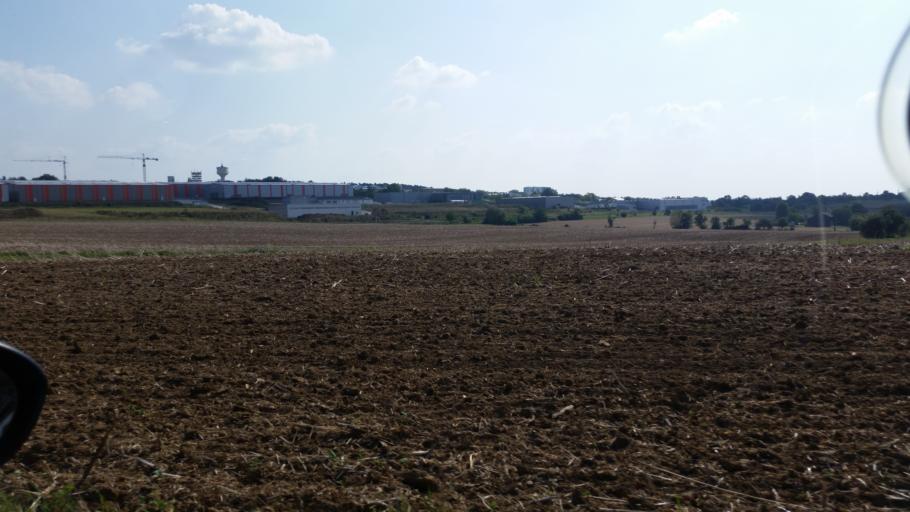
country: DE
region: Baden-Wuerttemberg
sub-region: Karlsruhe Region
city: Osterburken
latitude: 49.4290
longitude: 9.4503
